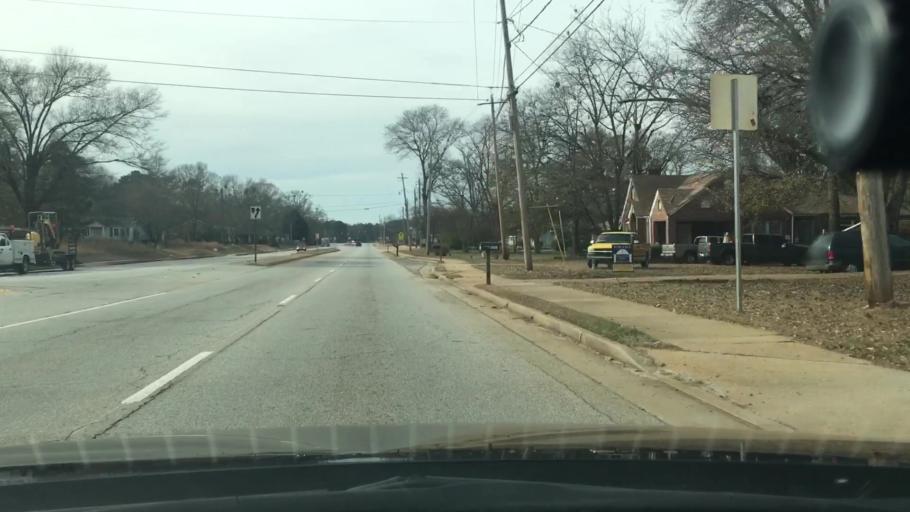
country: US
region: Georgia
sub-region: Spalding County
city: Experiment
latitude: 33.2734
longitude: -84.3006
